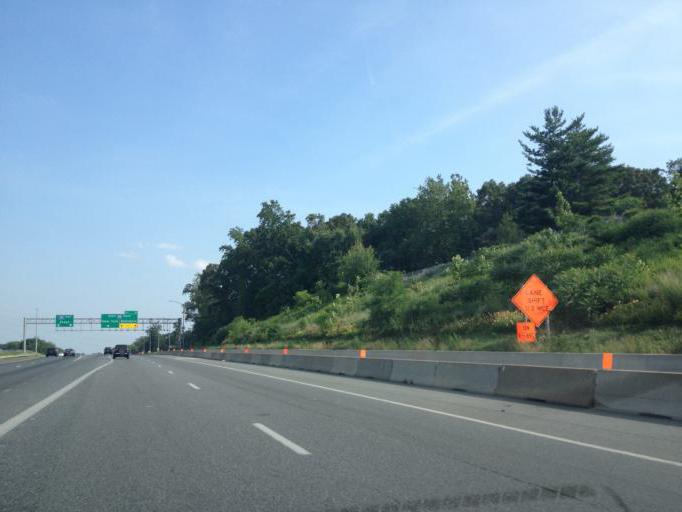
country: US
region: Maryland
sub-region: Baltimore County
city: Overlea
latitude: 39.3608
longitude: -76.5056
